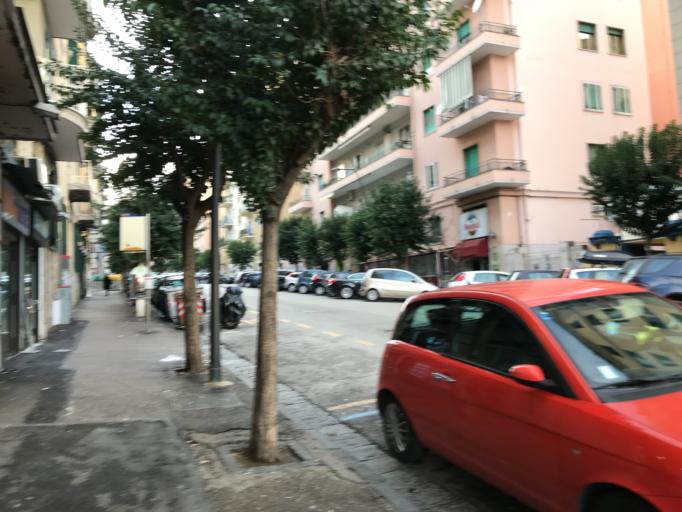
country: IT
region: Campania
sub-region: Provincia di Napoli
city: Napoli
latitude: 40.8505
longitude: 14.2300
